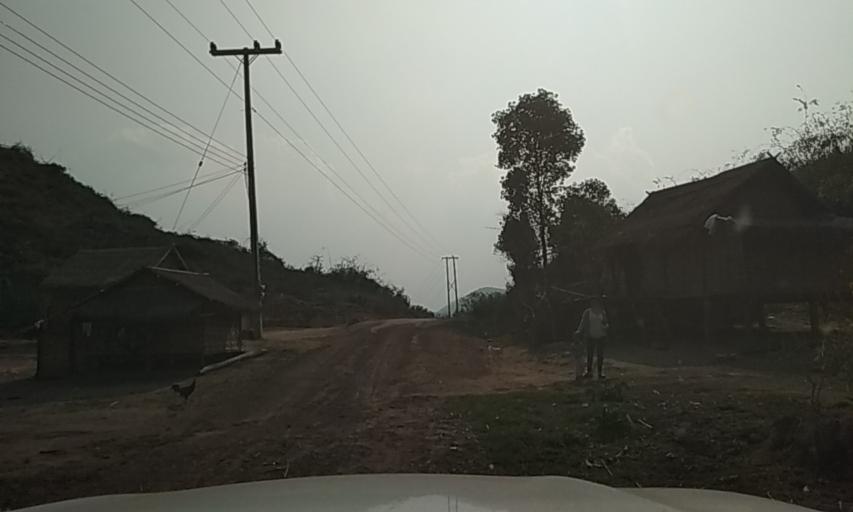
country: LA
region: Louangphabang
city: Louangphabang
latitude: 20.0405
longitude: 101.8011
